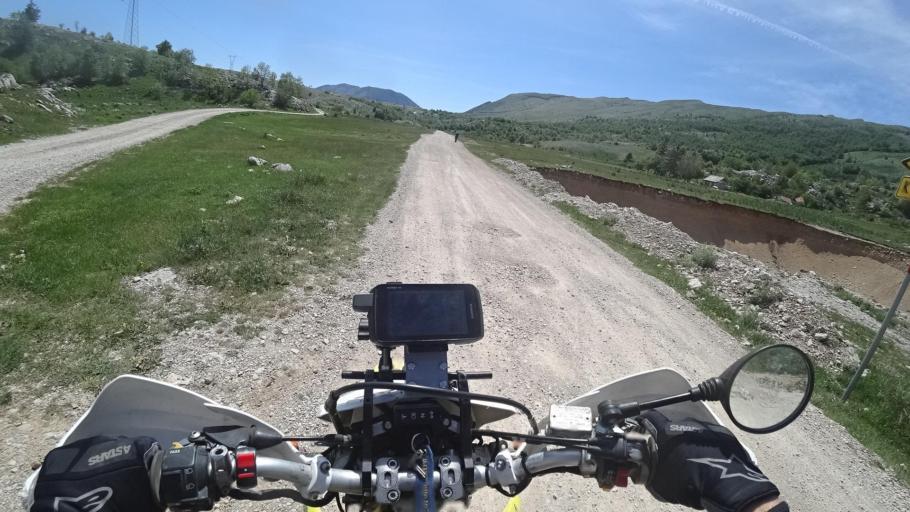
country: BA
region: Federation of Bosnia and Herzegovina
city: Bijela
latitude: 43.5044
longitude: 18.0323
